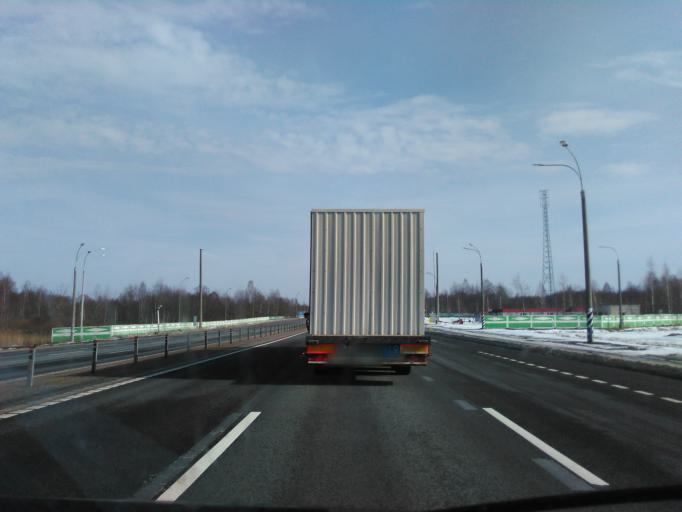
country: BY
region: Vitebsk
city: Dubrowna
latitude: 54.6901
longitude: 30.9453
